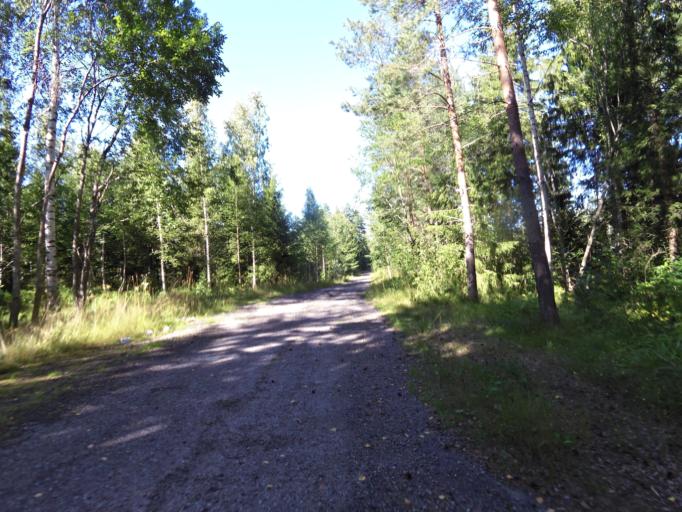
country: SE
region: Gaevleborg
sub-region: Sandvikens Kommun
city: Jarbo
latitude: 60.5630
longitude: 16.4864
